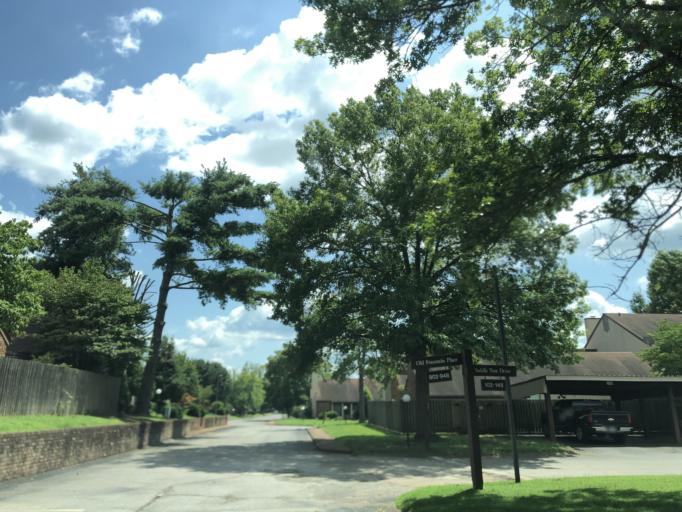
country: US
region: Tennessee
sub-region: Davidson County
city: Lakewood
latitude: 36.2245
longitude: -86.5958
